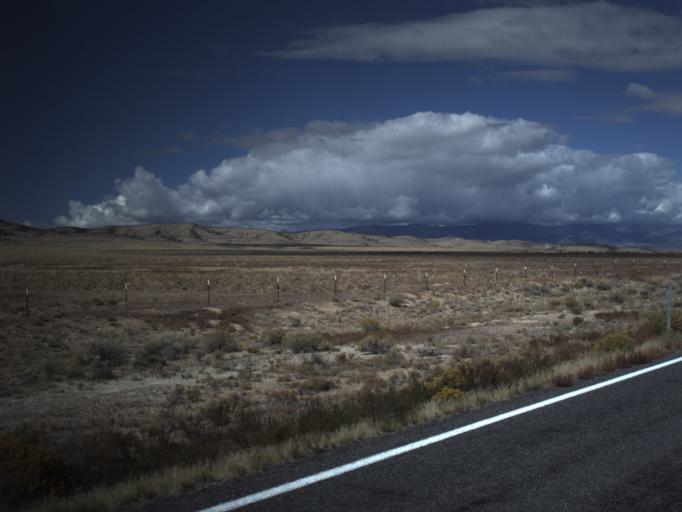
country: US
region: Utah
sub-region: Beaver County
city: Milford
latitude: 38.6658
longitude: -113.8809
